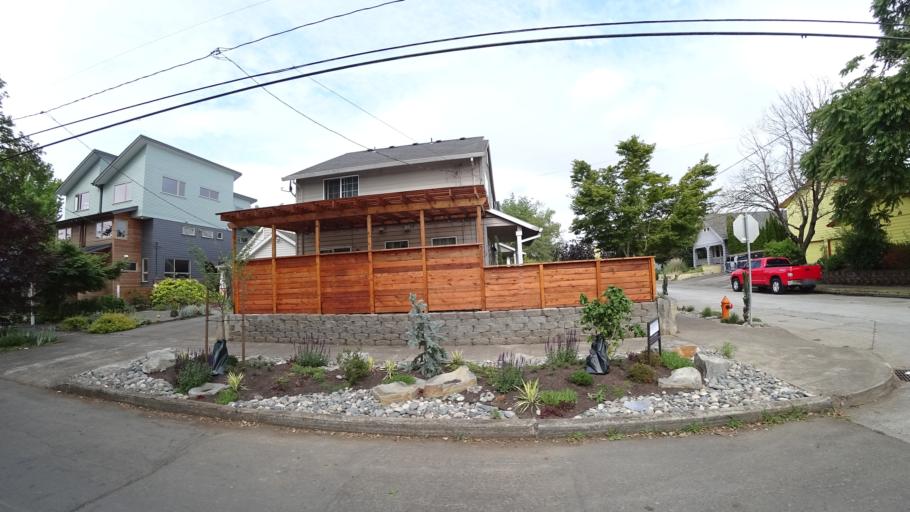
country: US
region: Oregon
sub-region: Multnomah County
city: Portland
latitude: 45.5676
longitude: -122.6840
